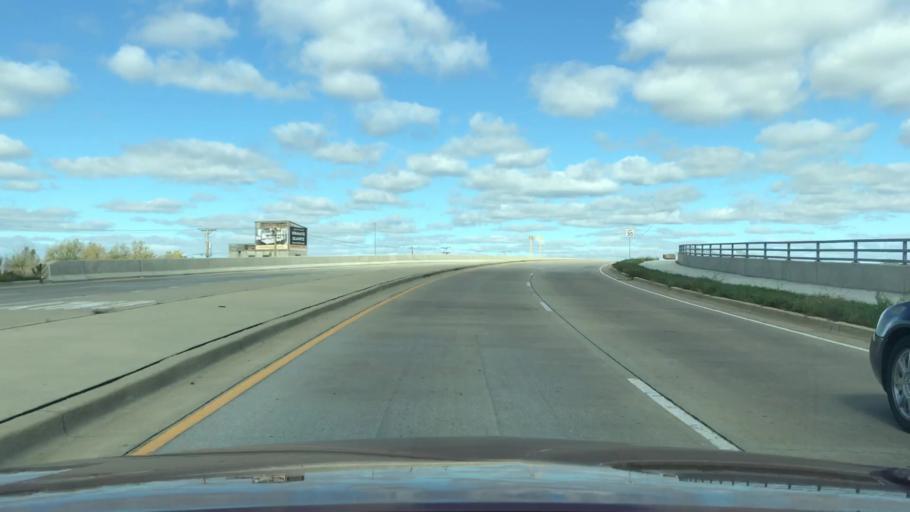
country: US
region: Indiana
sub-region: Lake County
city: Dyer
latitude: 41.4965
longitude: -87.5285
